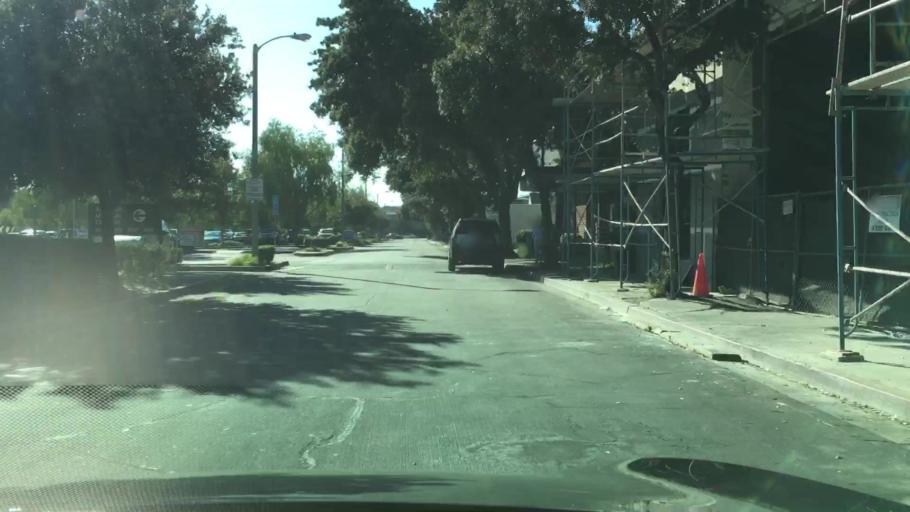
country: US
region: California
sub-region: Los Angeles County
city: Arcadia
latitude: 34.1413
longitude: -118.0291
